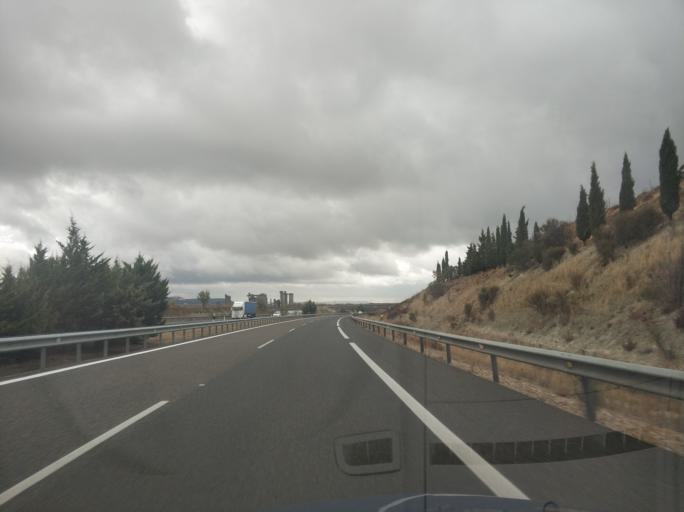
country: ES
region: Castille and Leon
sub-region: Provincia de Palencia
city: Soto de Cerrato
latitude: 41.9560
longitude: -4.4594
